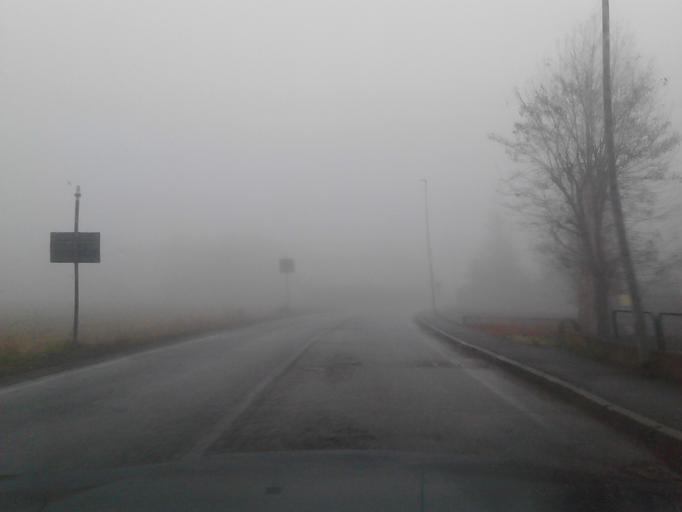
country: IT
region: Lombardy
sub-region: Provincia di Bergamo
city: Telgate
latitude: 45.6326
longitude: 9.8511
